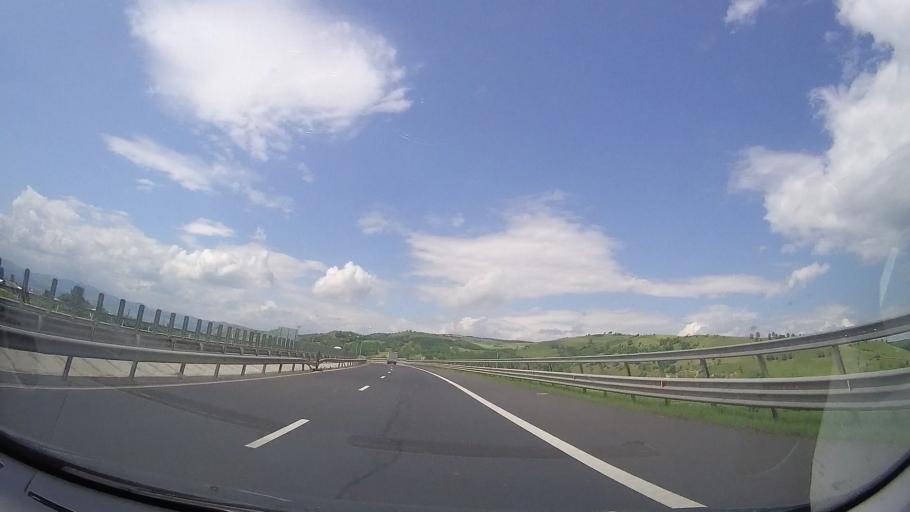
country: RO
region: Alba
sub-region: Municipiul Sebes
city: Sebes
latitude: 45.9639
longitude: 23.5962
